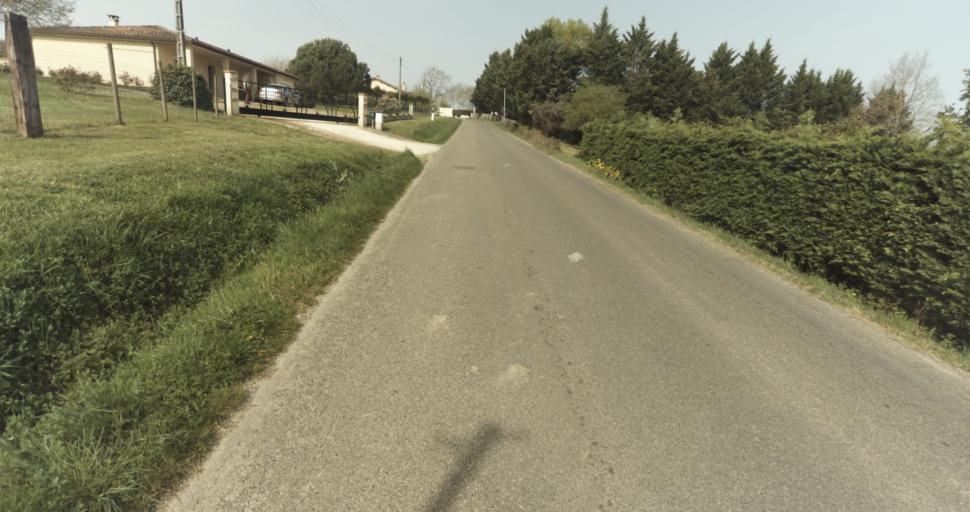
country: FR
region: Midi-Pyrenees
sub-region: Departement du Tarn-et-Garonne
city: Moissac
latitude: 44.1206
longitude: 1.0915
